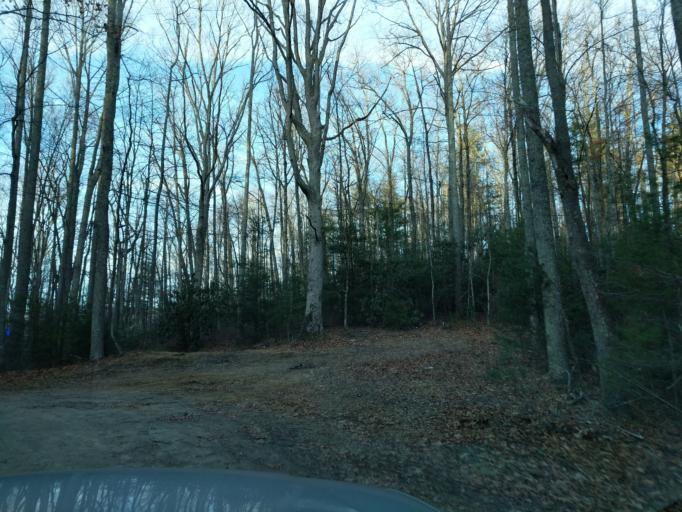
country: US
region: North Carolina
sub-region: Haywood County
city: Cove Creek
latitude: 35.7441
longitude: -83.0541
